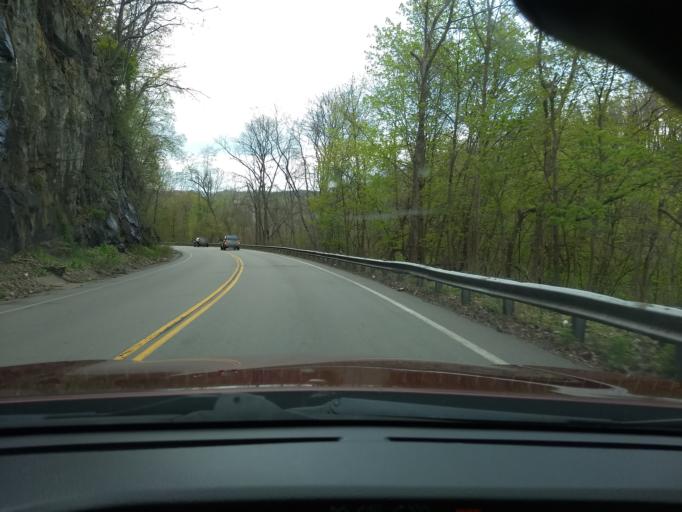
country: US
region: Pennsylvania
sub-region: Allegheny County
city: East McKeesport
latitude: 40.3891
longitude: -79.7985
